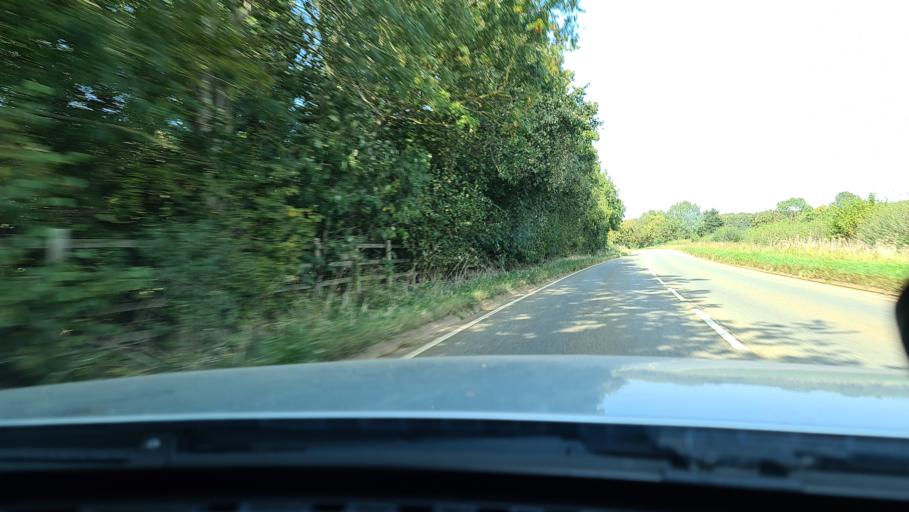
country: GB
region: England
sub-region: Oxfordshire
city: Hanwell
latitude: 52.0836
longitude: -1.3714
